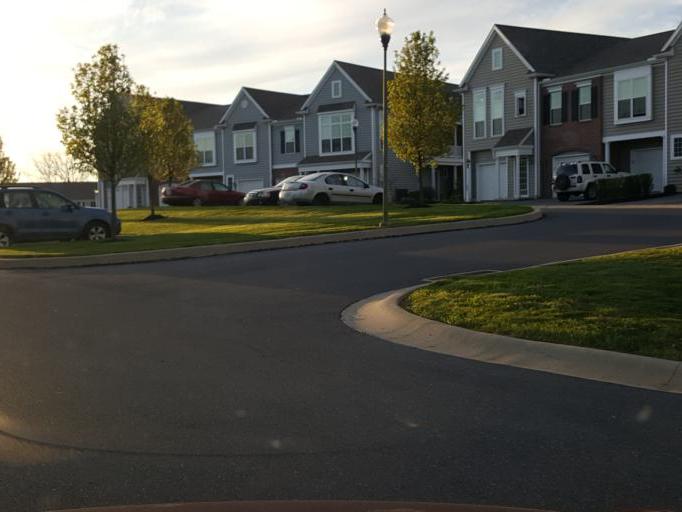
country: US
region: Pennsylvania
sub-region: Dauphin County
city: Hummelstown
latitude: 40.2491
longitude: -76.7144
